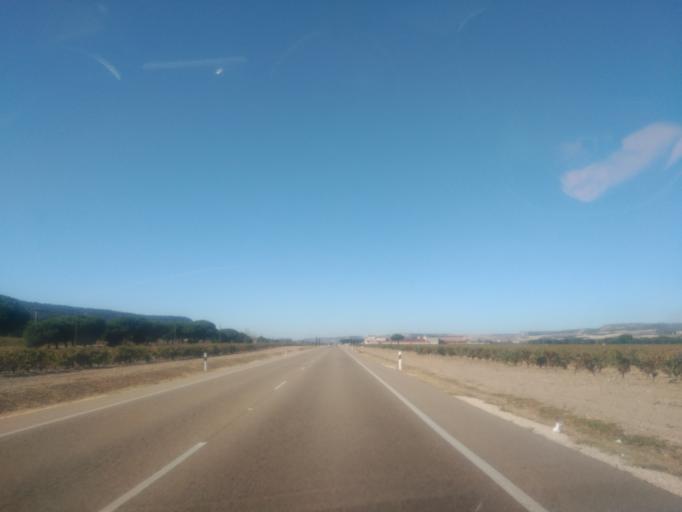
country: ES
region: Castille and Leon
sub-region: Provincia de Valladolid
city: Valbuena de Duero
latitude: 41.6281
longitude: -4.3109
